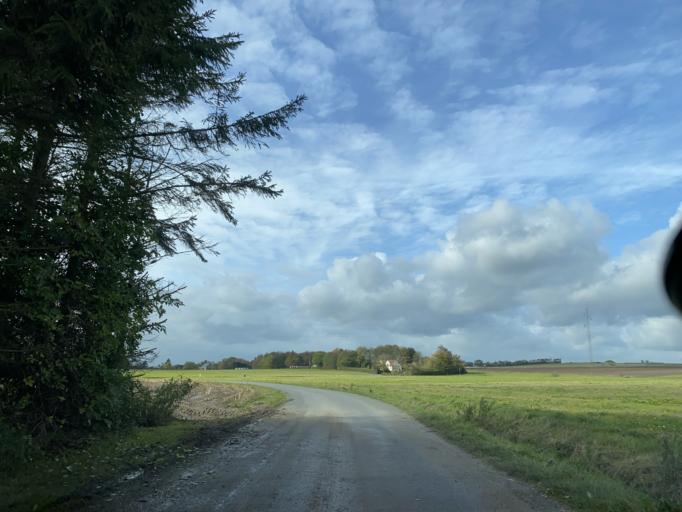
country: DK
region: Central Jutland
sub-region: Arhus Kommune
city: Sabro
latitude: 56.1951
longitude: 9.9993
